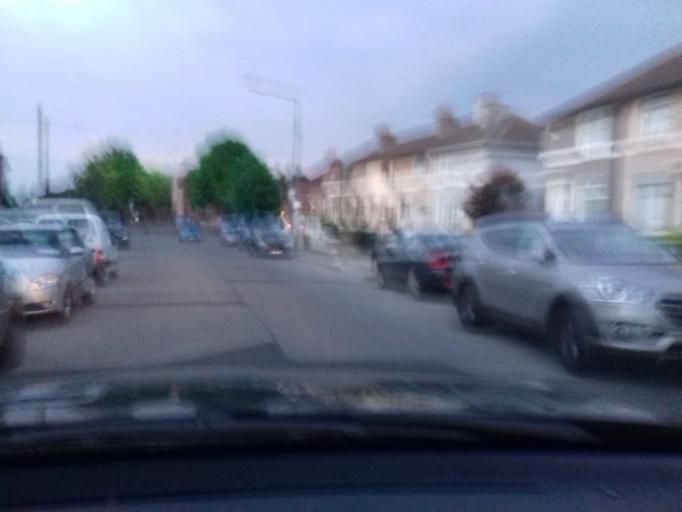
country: IE
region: Leinster
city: Crumlin
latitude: 53.3305
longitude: -6.3211
